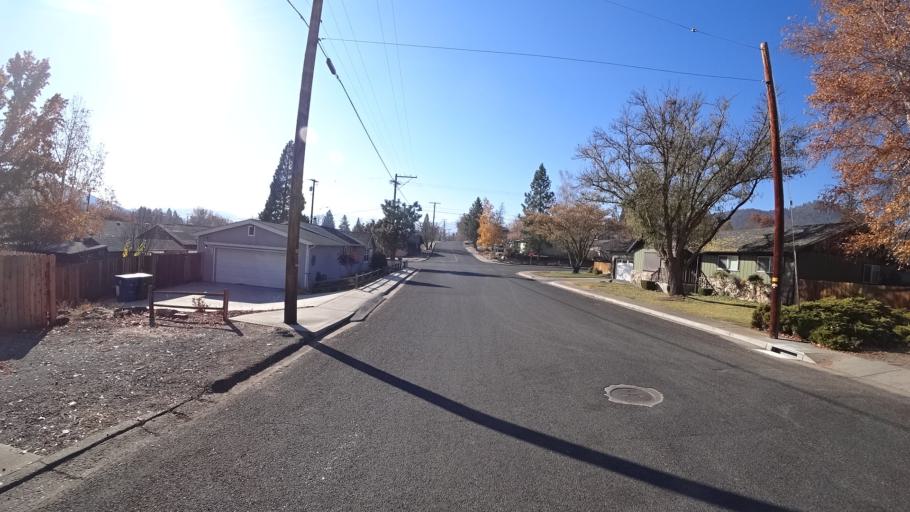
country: US
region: California
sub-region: Siskiyou County
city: Yreka
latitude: 41.7343
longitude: -122.6458
